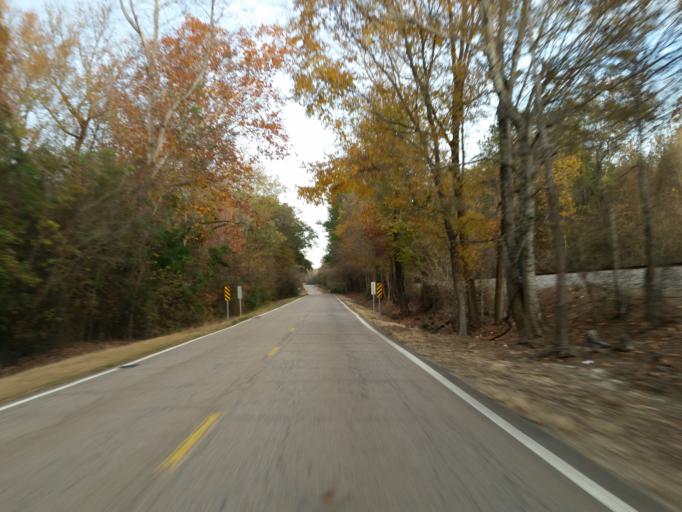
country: US
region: Alabama
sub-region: Sumter County
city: York
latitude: 32.4239
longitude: -88.4271
